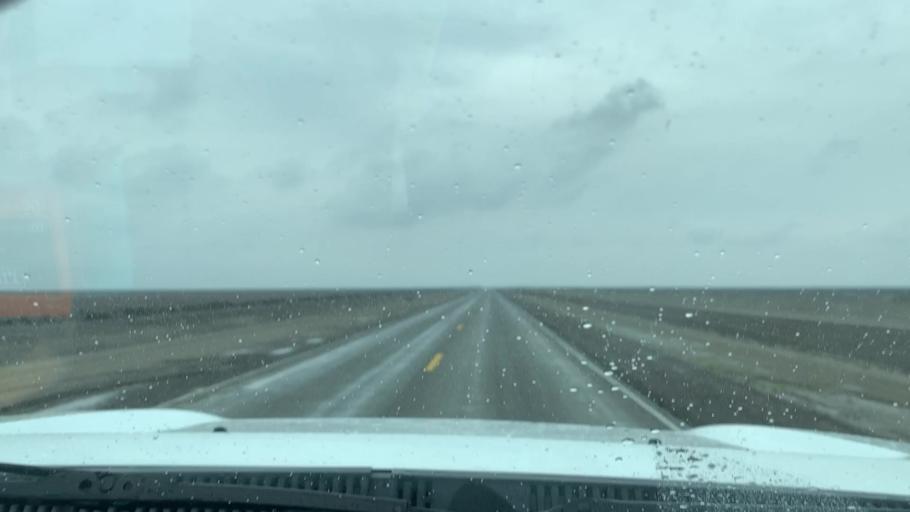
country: US
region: California
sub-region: Tulare County
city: Alpaugh
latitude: 35.9343
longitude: -119.5981
